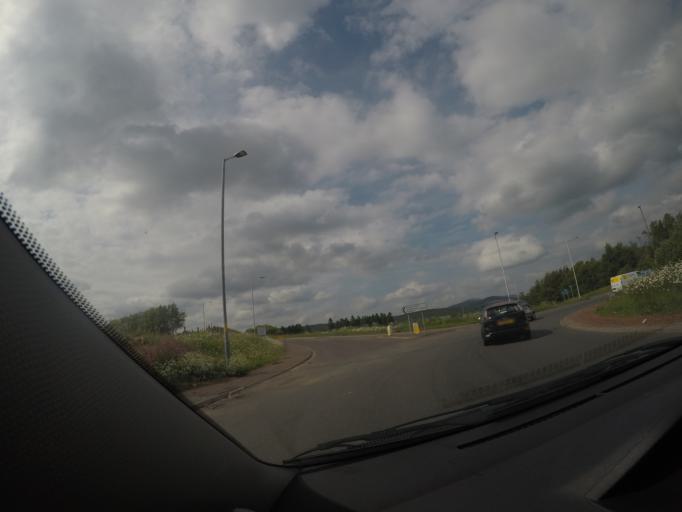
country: GB
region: Scotland
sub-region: South Lanarkshire
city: Douglas
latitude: 55.5029
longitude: -3.6976
